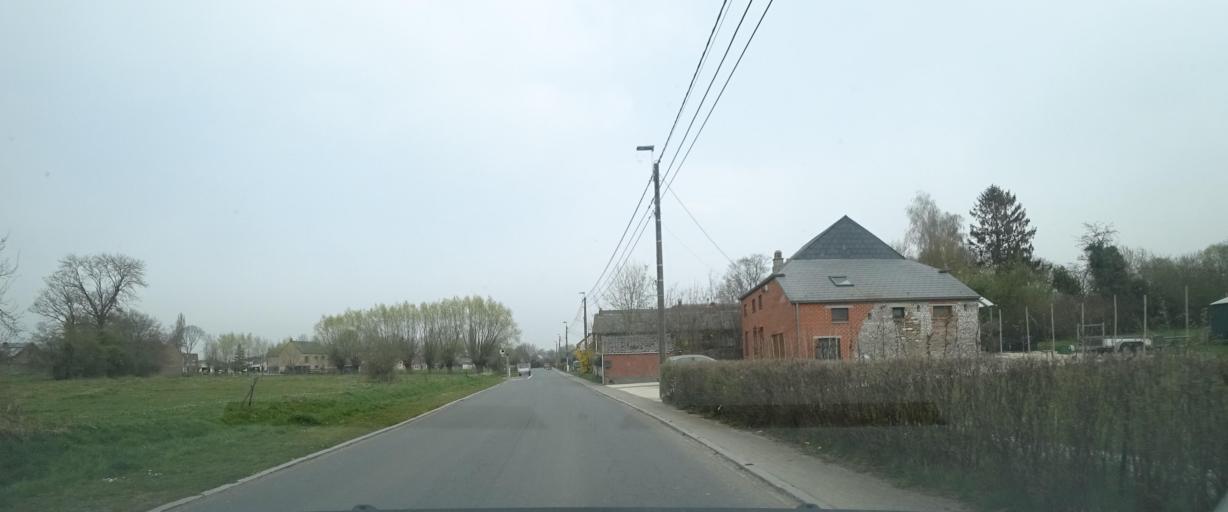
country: BE
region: Wallonia
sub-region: Province du Brabant Wallon
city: Walhain-Saint-Paul
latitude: 50.6217
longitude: 4.6965
